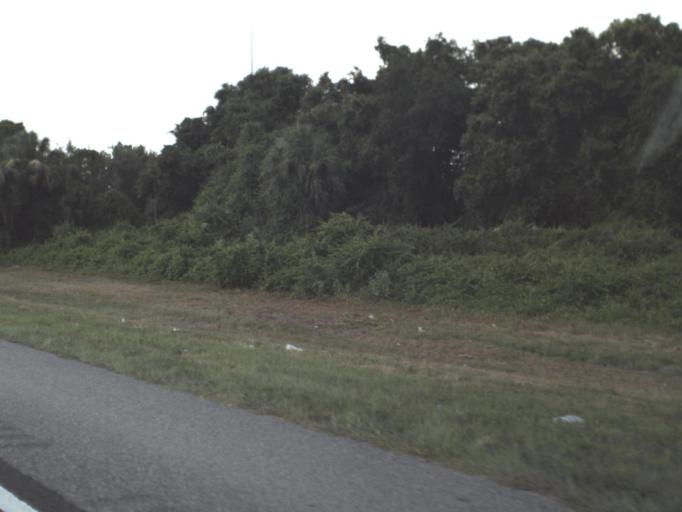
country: US
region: Florida
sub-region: Hillsborough County
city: Riverview
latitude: 27.8504
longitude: -82.3468
